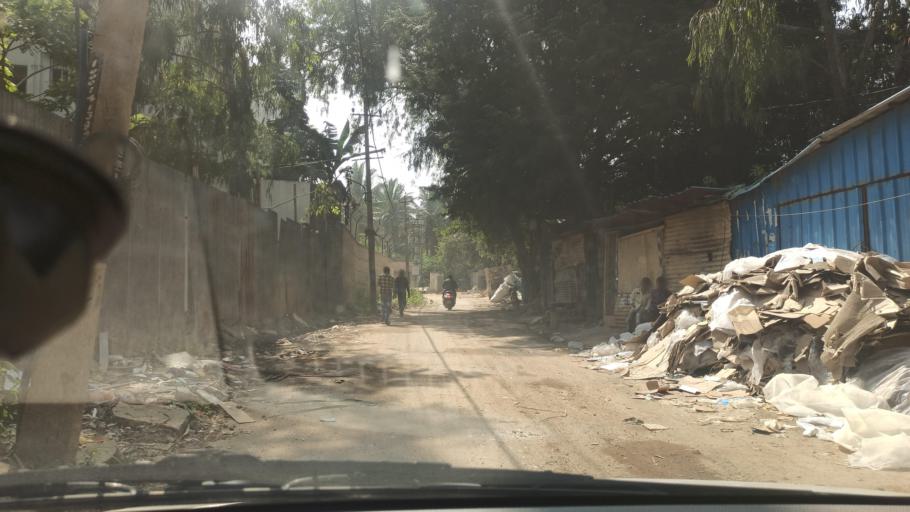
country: IN
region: Karnataka
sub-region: Bangalore Urban
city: Bangalore
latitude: 12.9362
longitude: 77.6881
